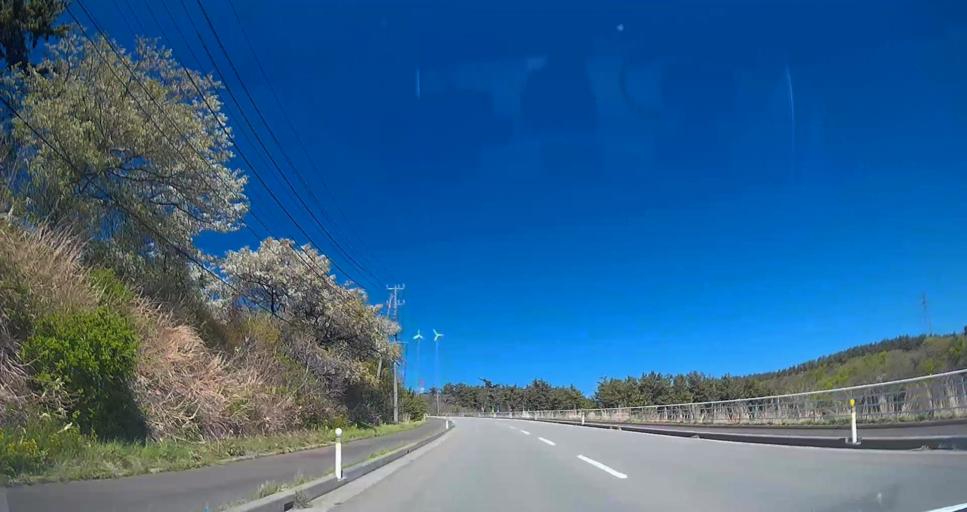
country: JP
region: Hokkaido
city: Hakodate
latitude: 41.5051
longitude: 140.9141
